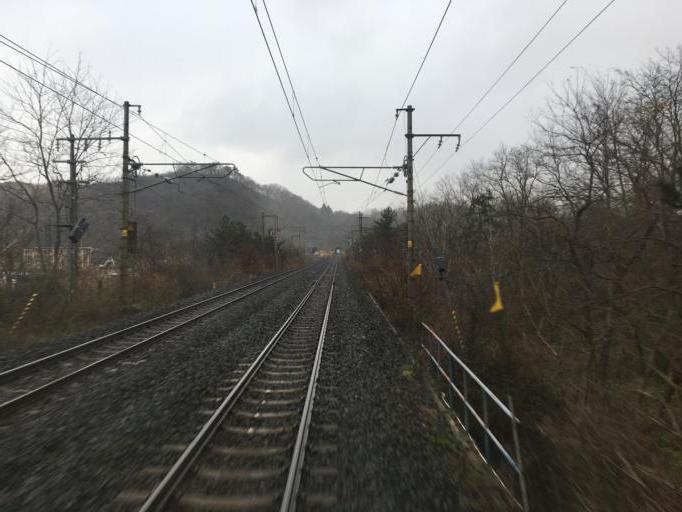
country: JP
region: Aomori
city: Aomori Shi
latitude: 40.8643
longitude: 140.8335
